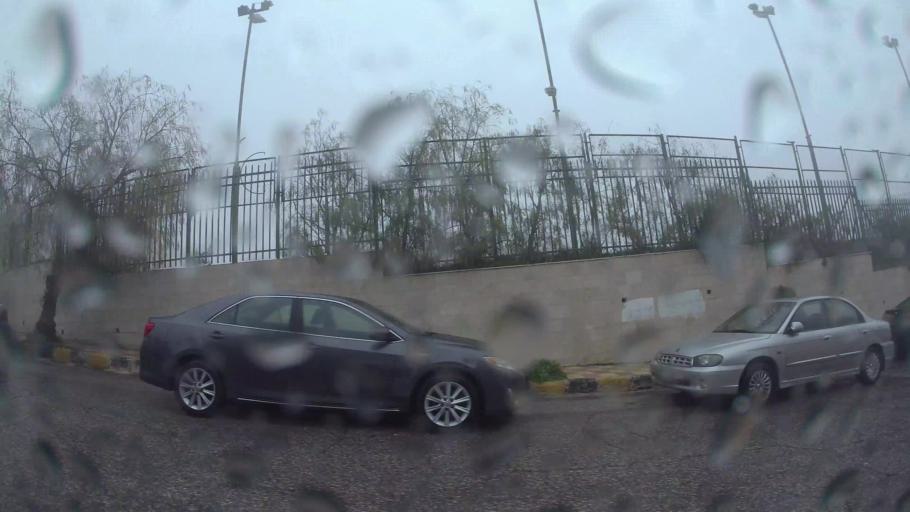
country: JO
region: Amman
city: Al Jubayhah
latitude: 32.0133
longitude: 35.8839
